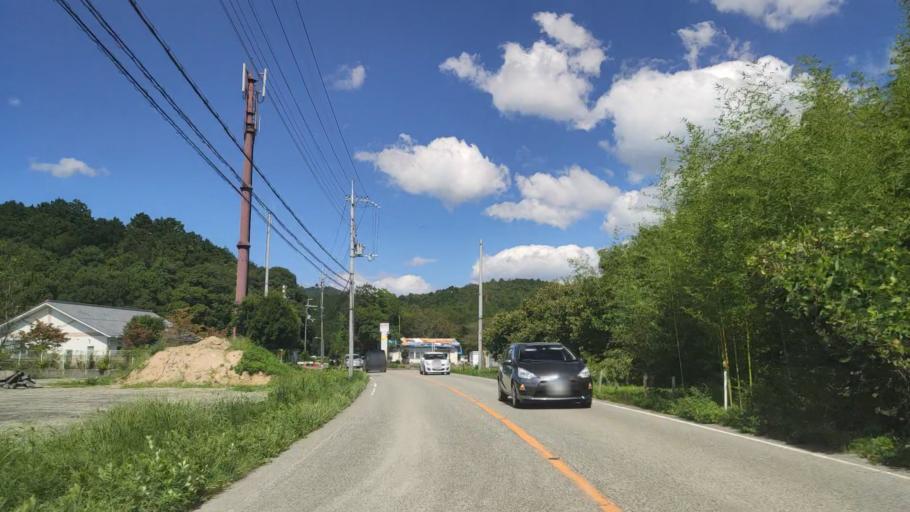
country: JP
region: Kyoto
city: Fukuchiyama
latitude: 35.1853
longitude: 135.1240
